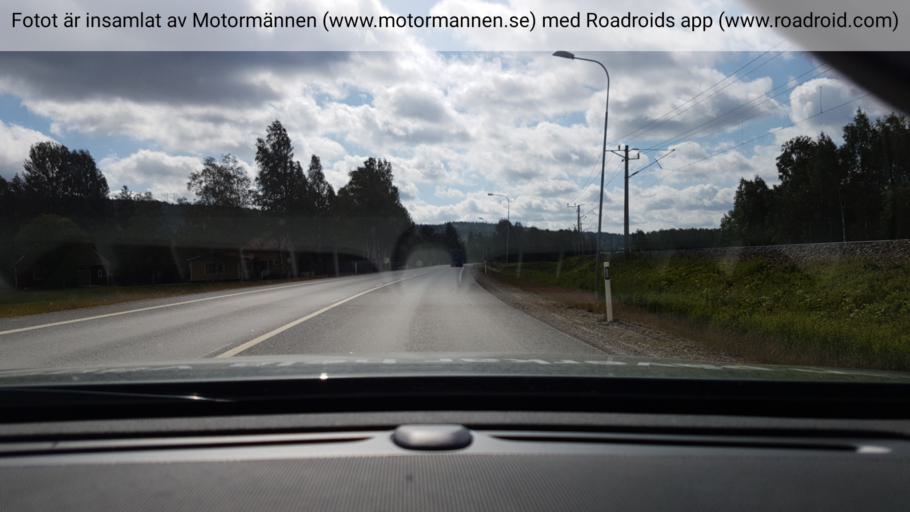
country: SE
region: Vaesterbotten
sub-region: Vannas Kommun
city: Vannasby
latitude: 63.9209
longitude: 19.8681
